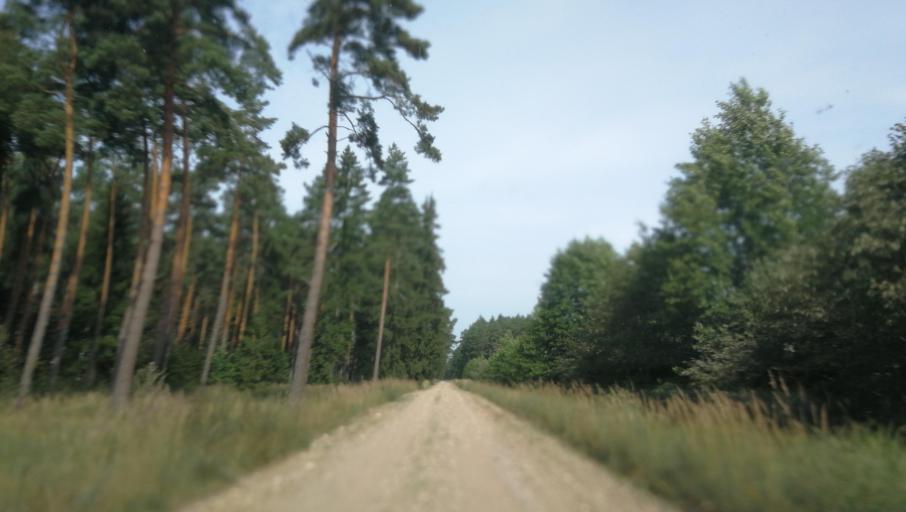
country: LV
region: Pavilostas
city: Pavilosta
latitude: 56.8252
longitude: 21.2878
